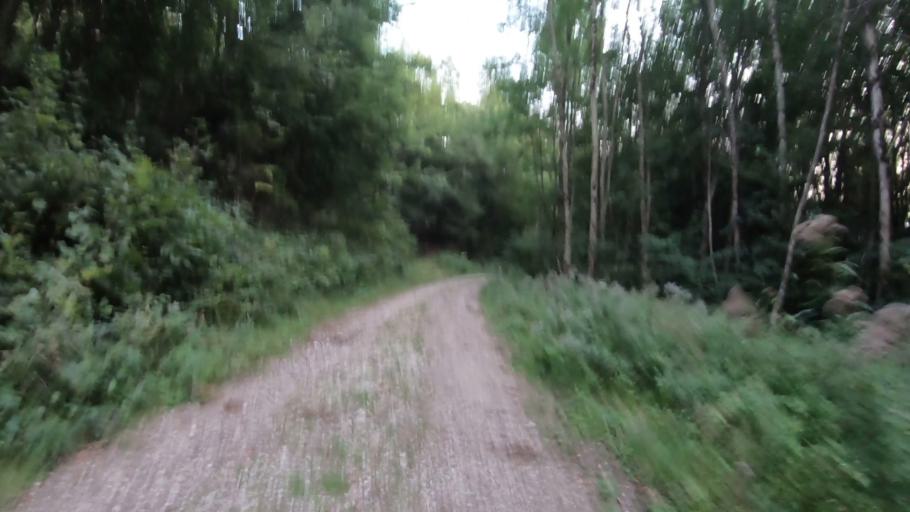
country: DE
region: Bavaria
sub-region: Upper Bavaria
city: Ruhpolding
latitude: 47.7746
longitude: 12.6580
